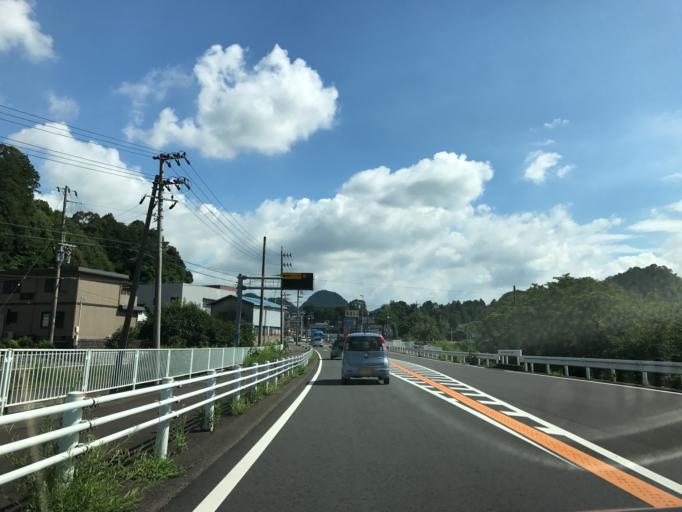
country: JP
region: Gifu
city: Mino
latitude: 35.5567
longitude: 136.9137
